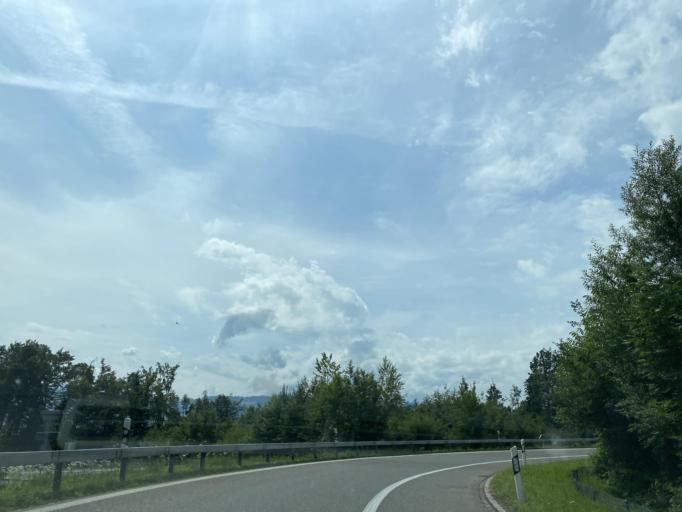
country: CH
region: Zurich
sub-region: Bezirk Hinwil
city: Rueti / Dorfzentrum, Suedl. Teil
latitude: 47.2303
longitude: 8.8684
